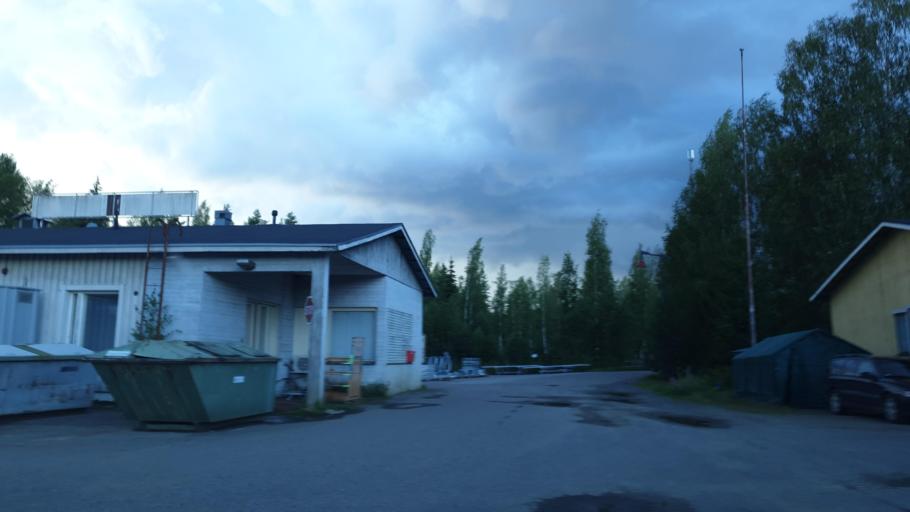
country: FI
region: Northern Savo
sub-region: Varkaus
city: Leppaevirta
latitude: 62.5807
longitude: 27.6077
